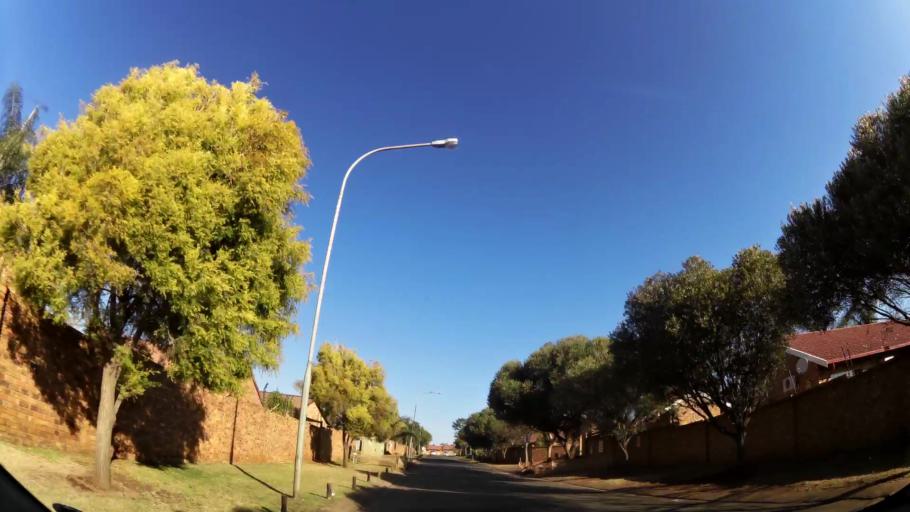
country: ZA
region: Gauteng
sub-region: City of Tshwane Metropolitan Municipality
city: Centurion
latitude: -25.8789
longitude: 28.1421
